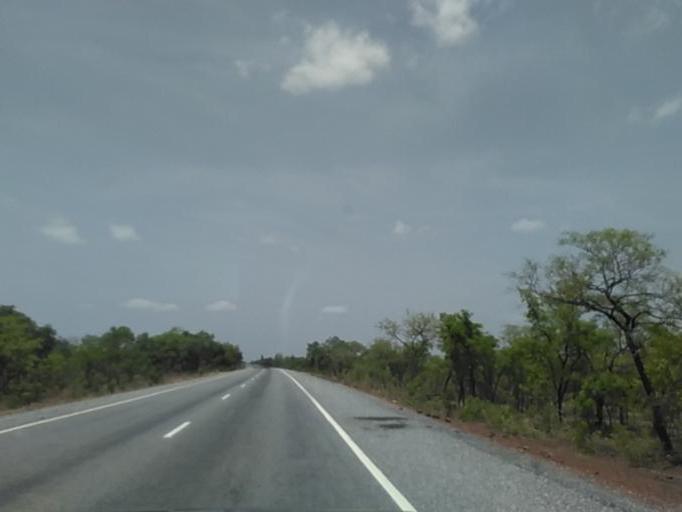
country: GH
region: Northern
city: Tamale
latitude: 9.1459
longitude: -1.3710
